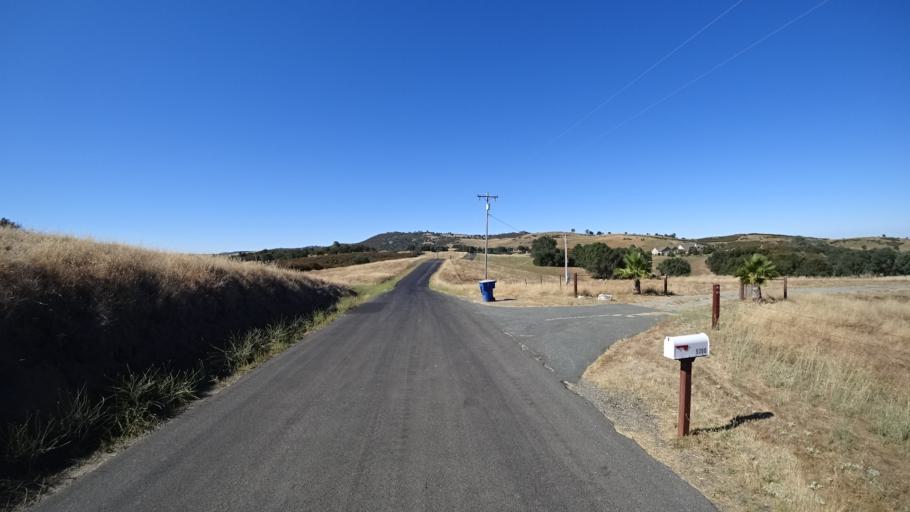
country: US
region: California
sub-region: Calaveras County
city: Rancho Calaveras
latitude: 38.1368
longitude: -120.8125
